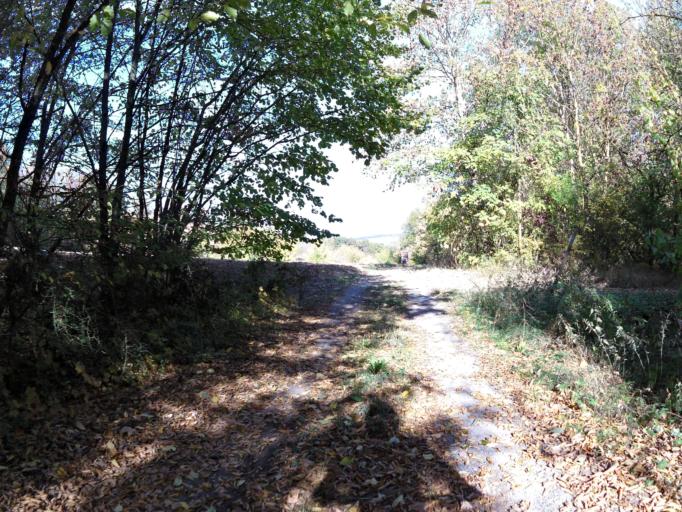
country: DE
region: Bavaria
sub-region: Regierungsbezirk Unterfranken
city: Eibelstadt
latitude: 49.7077
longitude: 9.9948
